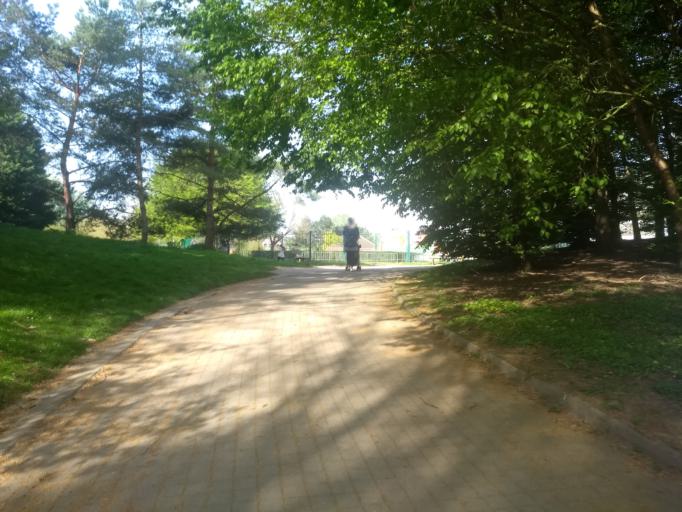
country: FR
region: Nord-Pas-de-Calais
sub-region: Departement du Pas-de-Calais
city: Sainte-Catherine
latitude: 50.3005
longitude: 2.7602
